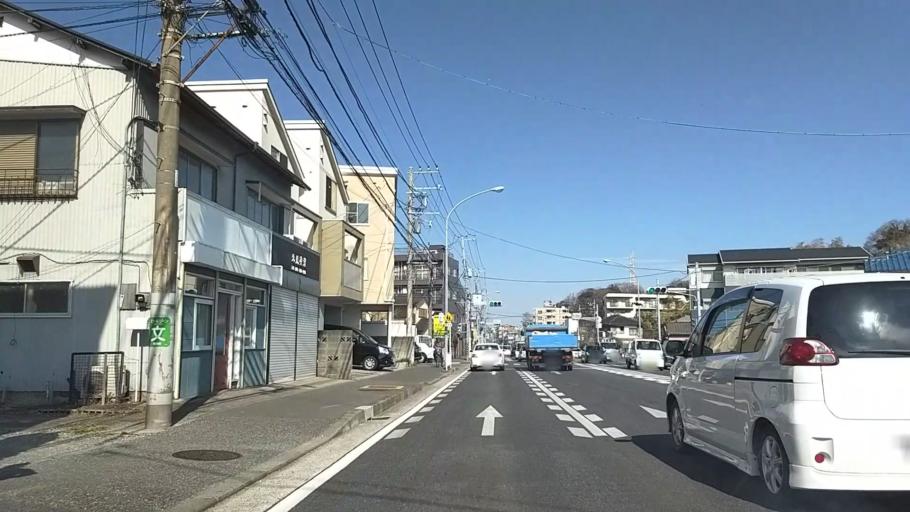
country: JP
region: Kanagawa
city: Yokohama
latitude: 35.3721
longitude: 139.6117
